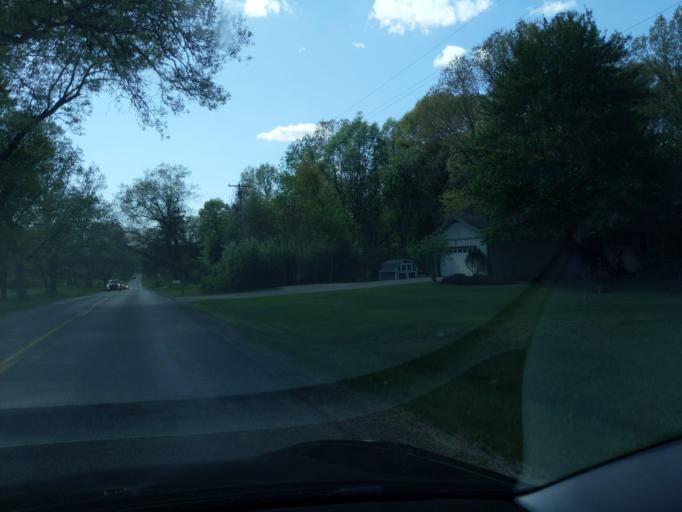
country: US
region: Michigan
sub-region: Kent County
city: Caledonia
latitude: 42.7979
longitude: -85.4449
